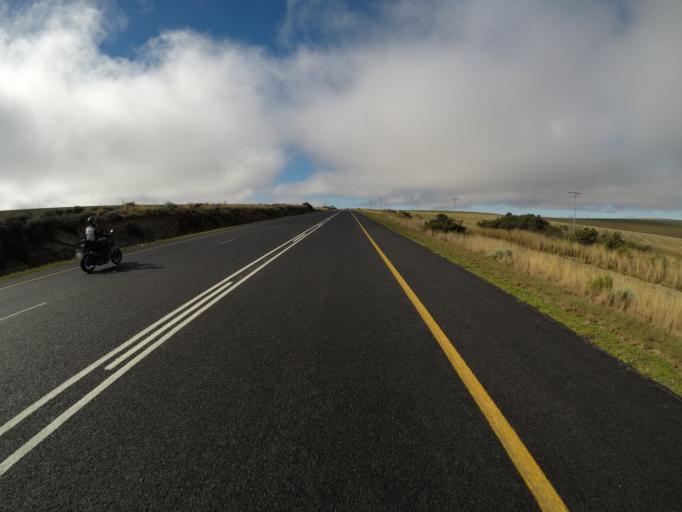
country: ZA
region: Western Cape
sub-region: Cape Winelands District Municipality
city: Ashton
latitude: -34.1578
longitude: 19.9547
